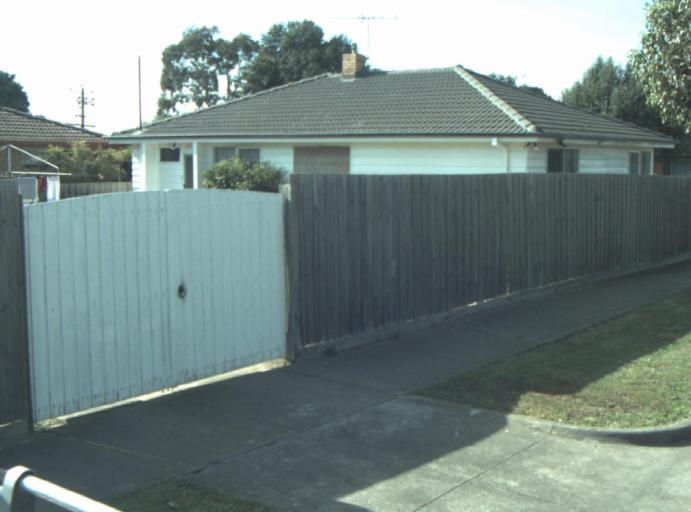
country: AU
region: Victoria
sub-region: Greater Geelong
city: Hamlyn Heights
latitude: -38.1224
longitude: 144.3213
